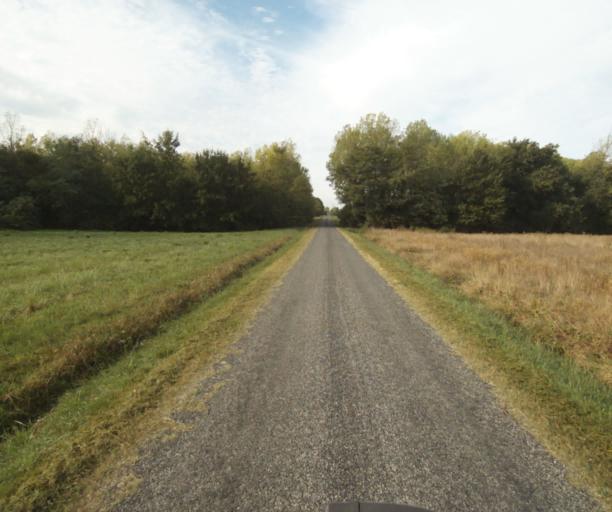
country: FR
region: Midi-Pyrenees
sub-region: Departement du Tarn-et-Garonne
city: Montech
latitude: 43.9730
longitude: 1.2388
